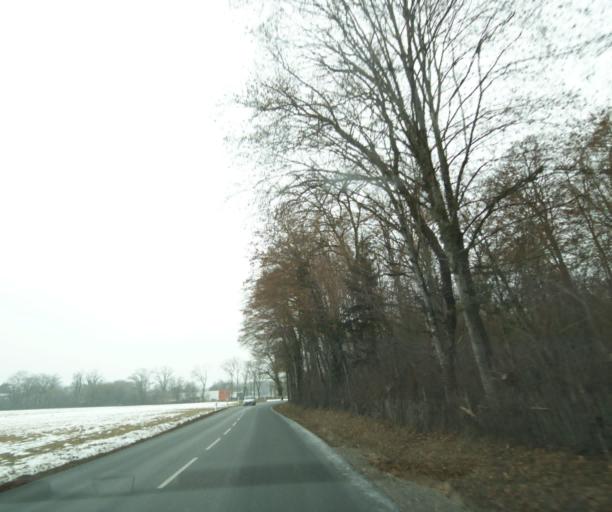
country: FR
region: Rhone-Alpes
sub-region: Departement de la Haute-Savoie
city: Contamine-sur-Arve
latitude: 46.1317
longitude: 6.3062
